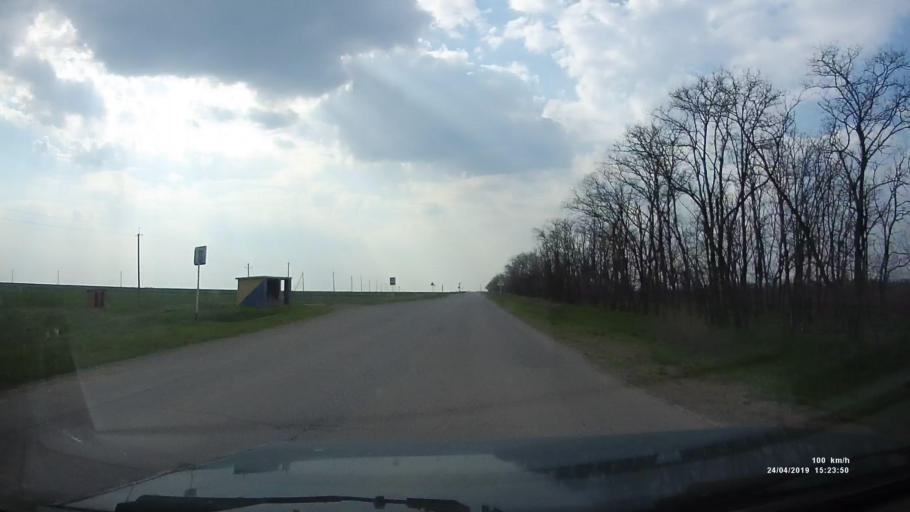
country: RU
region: Rostov
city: Remontnoye
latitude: 46.5444
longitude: 43.0818
